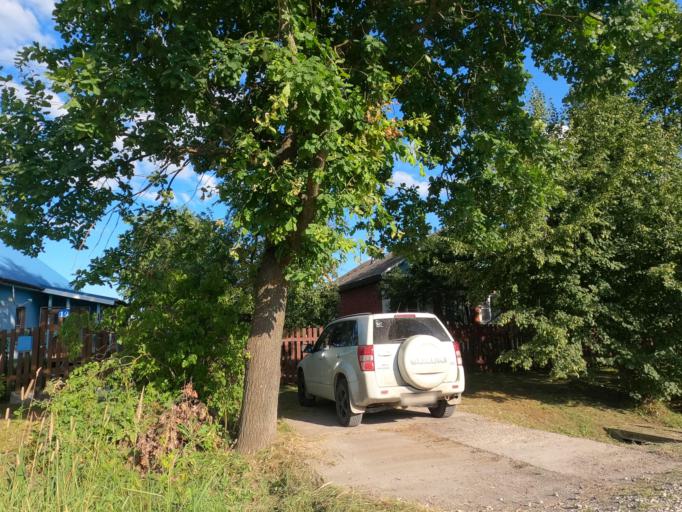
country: RU
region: Moskovskaya
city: Konobeyevo
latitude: 55.4102
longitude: 38.7183
